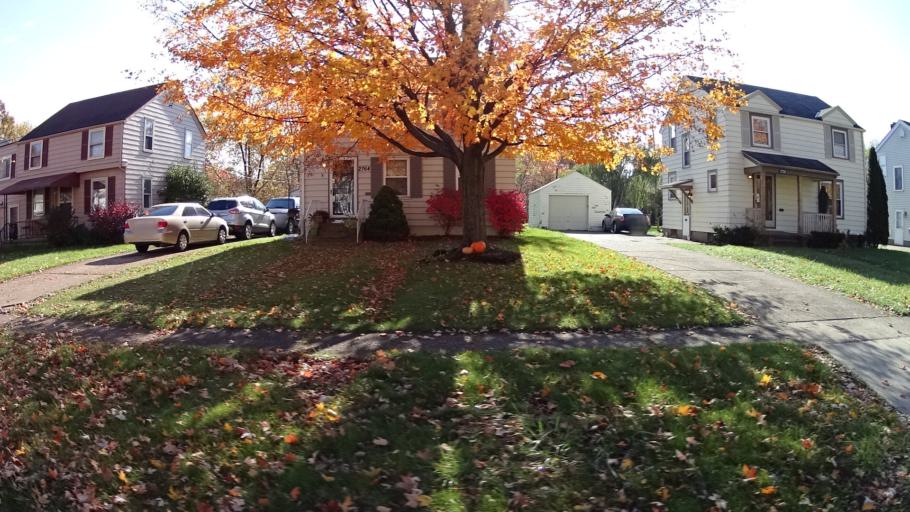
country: US
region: Ohio
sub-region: Lorain County
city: Sheffield Lake
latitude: 41.4766
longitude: -82.1423
